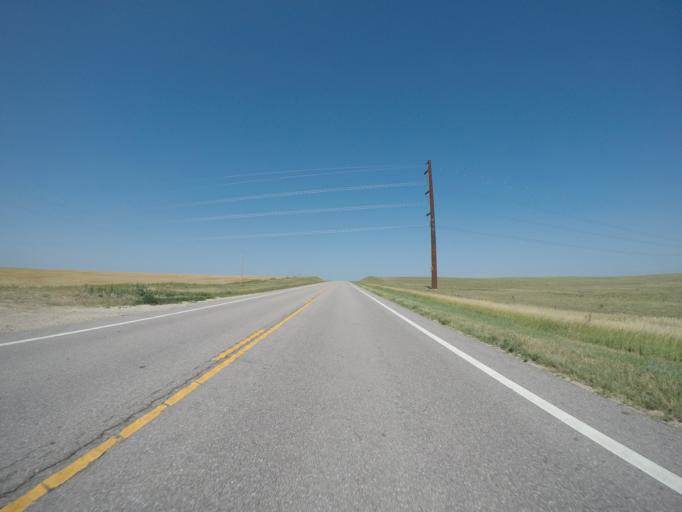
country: US
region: Kansas
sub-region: Cloud County
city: Concordia
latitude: 39.3647
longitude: -97.5600
